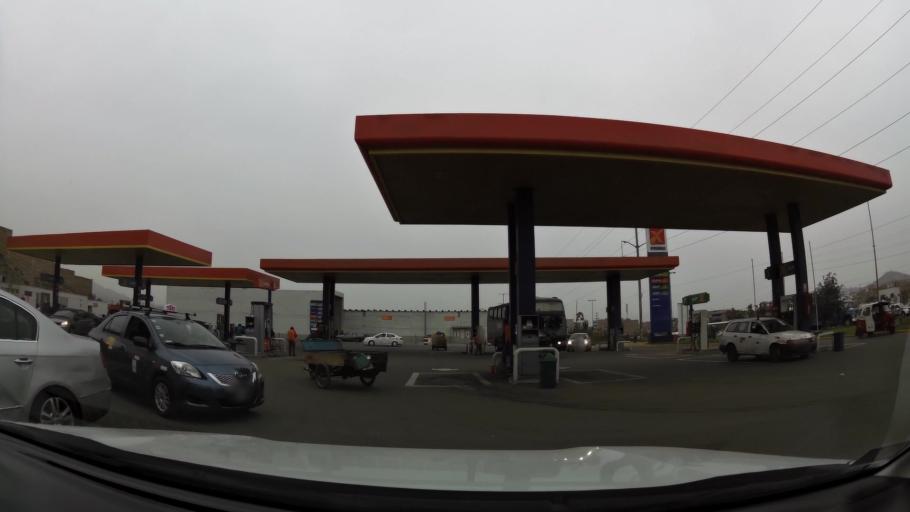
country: PE
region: Lima
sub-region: Lima
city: Surco
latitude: -12.1732
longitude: -76.9779
